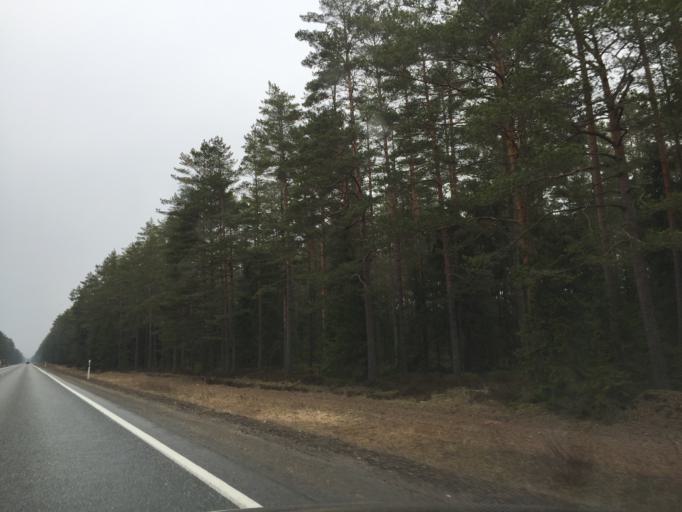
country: LV
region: Salacgrivas
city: Salacgriva
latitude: 57.5354
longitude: 24.4314
